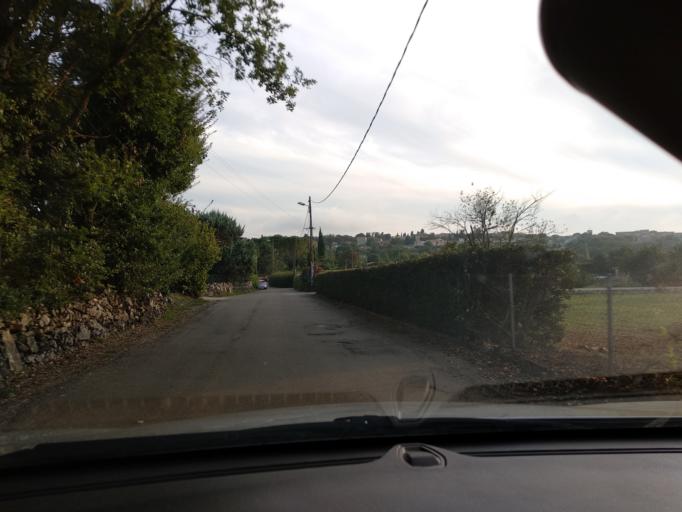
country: FR
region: Provence-Alpes-Cote d'Azur
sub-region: Departement des Alpes-Maritimes
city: Saint-Cezaire-sur-Siagne
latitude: 43.6542
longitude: 6.8008
